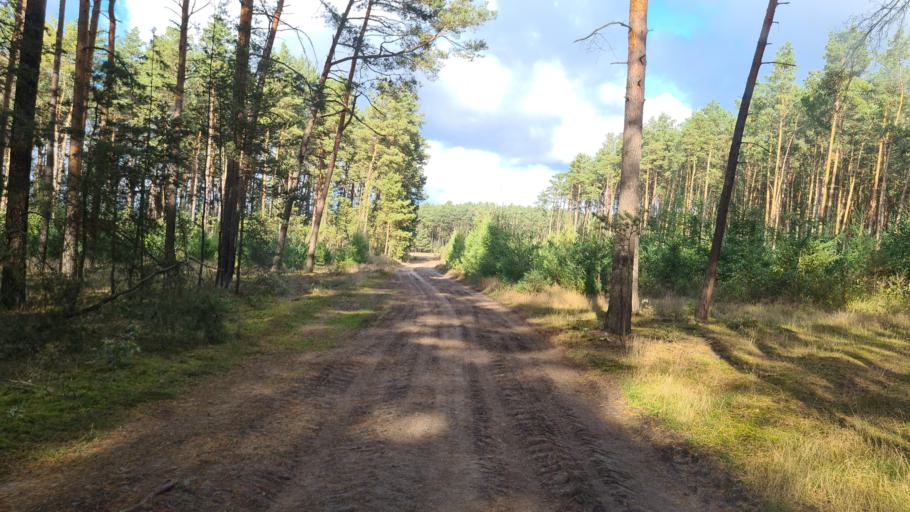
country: DE
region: Brandenburg
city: Vetschau
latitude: 51.7265
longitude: 14.0893
